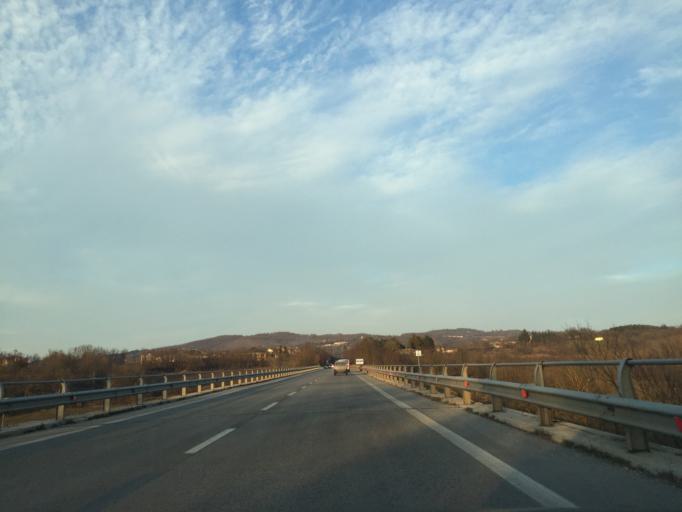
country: IT
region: Molise
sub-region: Provincia di Campobasso
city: Vinchiaturo
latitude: 41.4877
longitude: 14.5953
